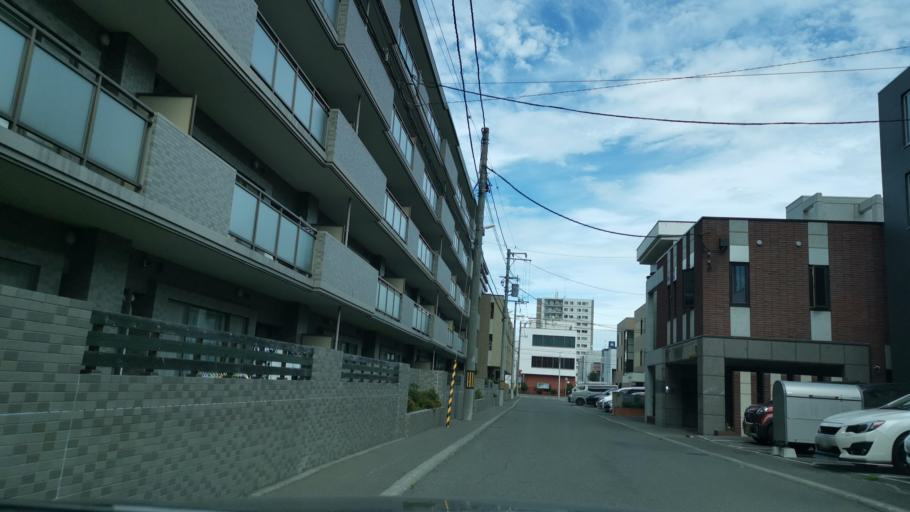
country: JP
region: Hokkaido
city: Sapporo
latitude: 43.0487
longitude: 141.3324
